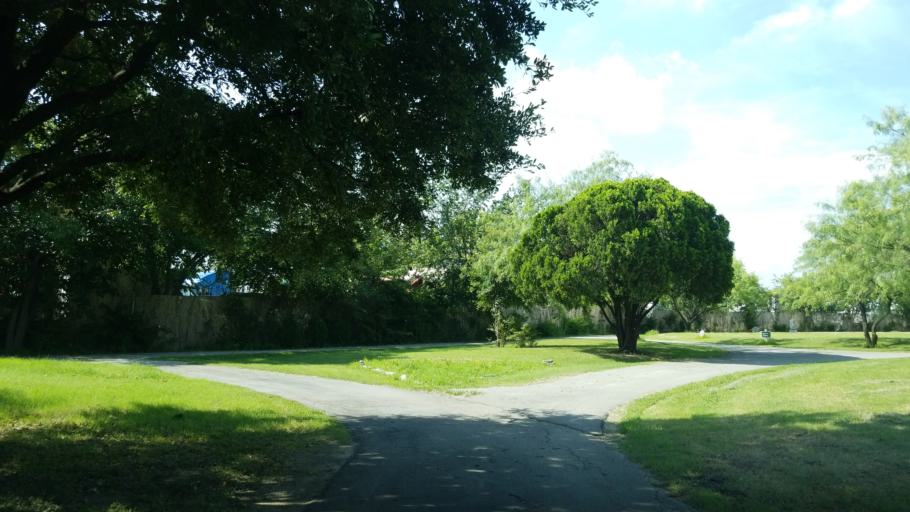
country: US
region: Texas
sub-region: Dallas County
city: Farmers Branch
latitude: 32.8781
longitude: -96.8878
